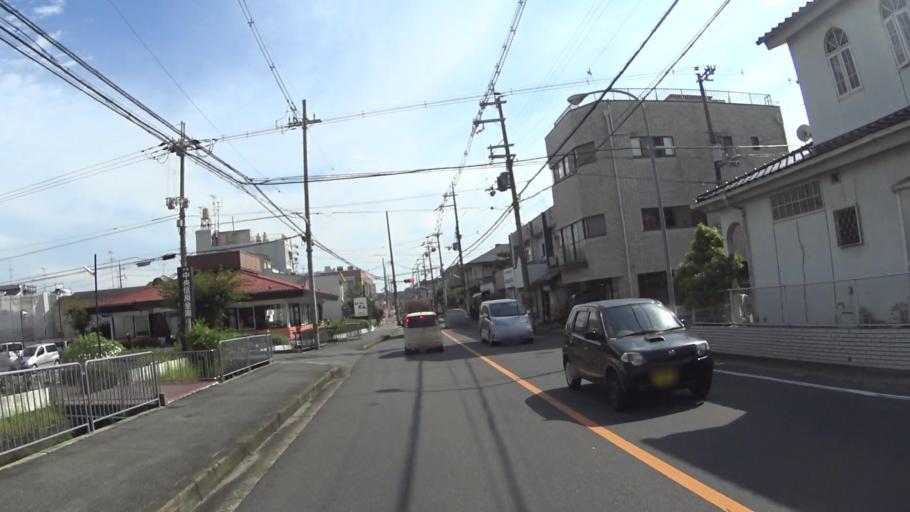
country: JP
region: Kyoto
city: Muko
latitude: 34.9708
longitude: 135.6941
